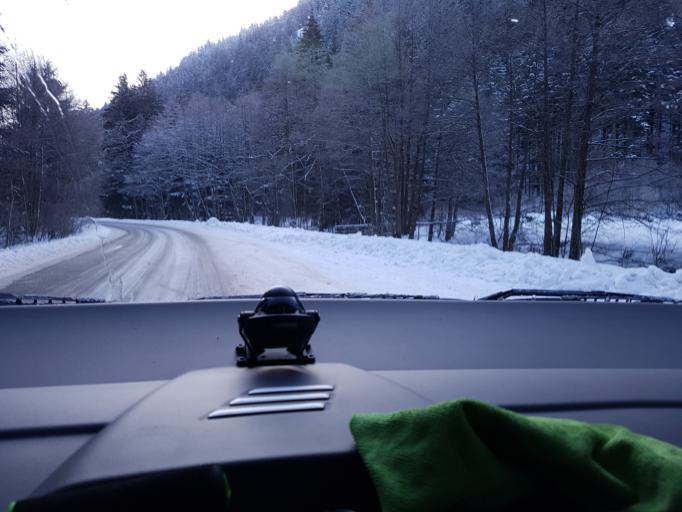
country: FR
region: Lorraine
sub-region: Departement des Vosges
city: Xonrupt-Longemer
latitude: 48.0625
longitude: 6.9613
